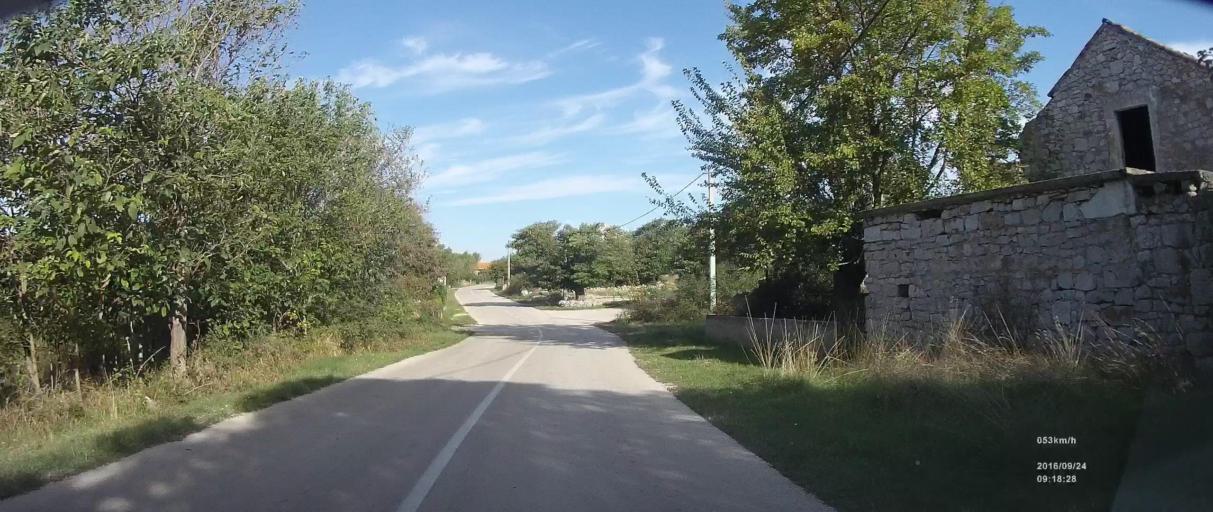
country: HR
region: Zadarska
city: Polaca
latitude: 44.0564
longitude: 15.5117
